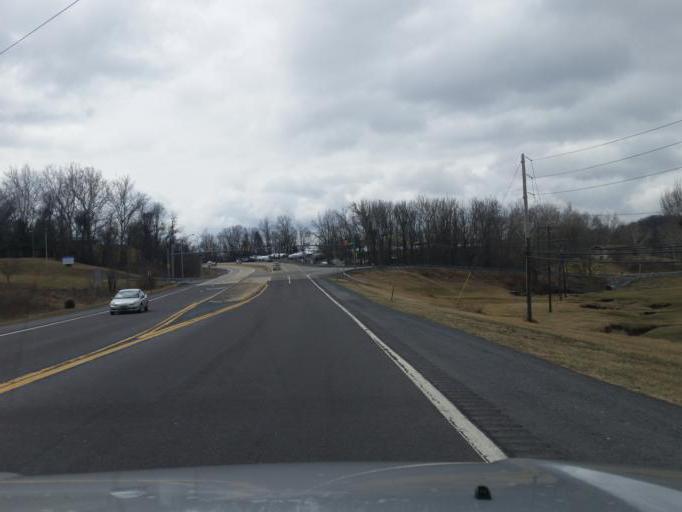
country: US
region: Pennsylvania
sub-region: Dauphin County
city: Middletown
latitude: 40.2313
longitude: -76.7176
